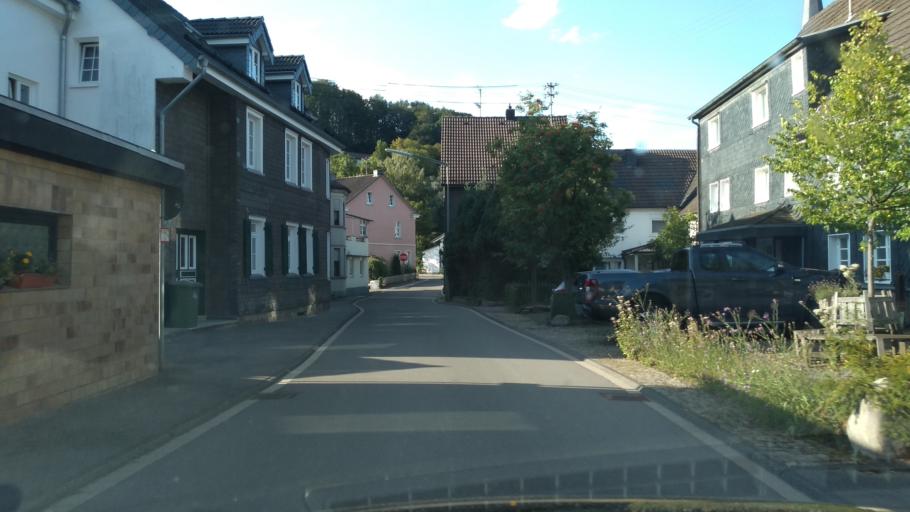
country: DE
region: North Rhine-Westphalia
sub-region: Regierungsbezirk Koln
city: Engelskirchen
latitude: 50.9933
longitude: 7.4618
